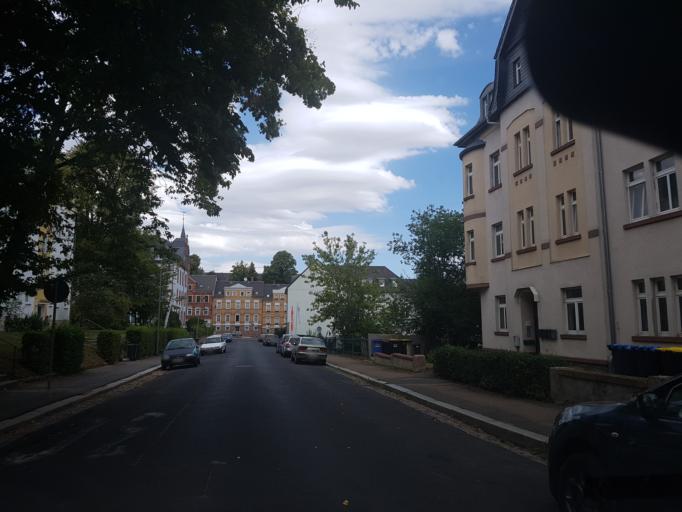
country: DE
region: Saxony
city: Waldheim
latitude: 51.0734
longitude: 13.0118
